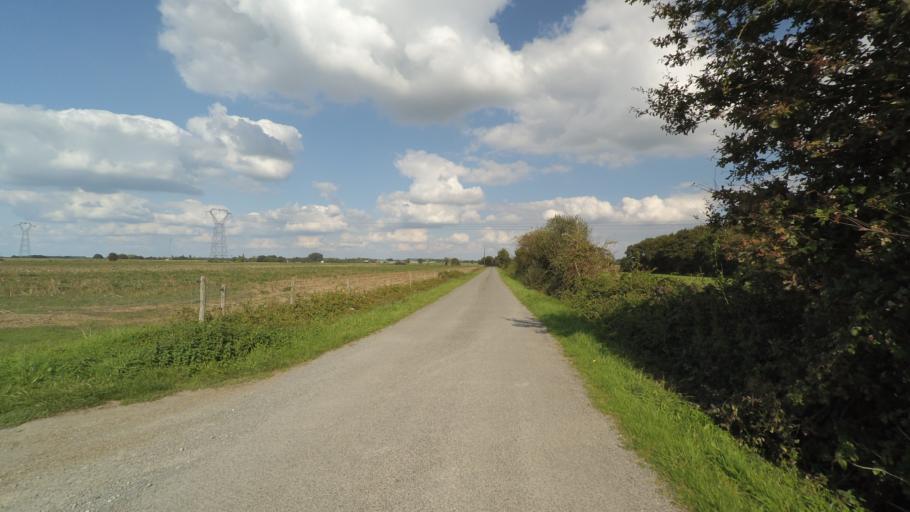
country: FR
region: Pays de la Loire
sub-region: Departement de la Loire-Atlantique
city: Vieillevigne
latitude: 46.9764
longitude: -1.4055
